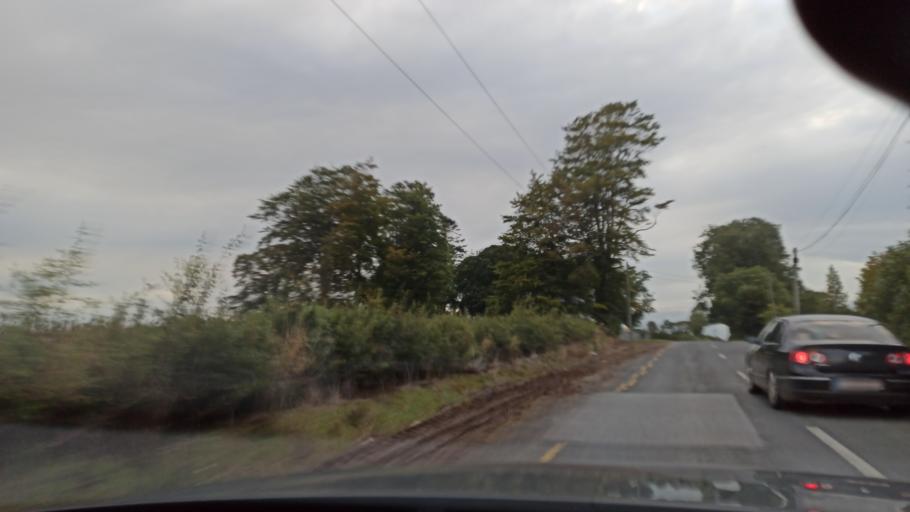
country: IE
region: Munster
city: Cashel
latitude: 52.4945
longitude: -7.8656
